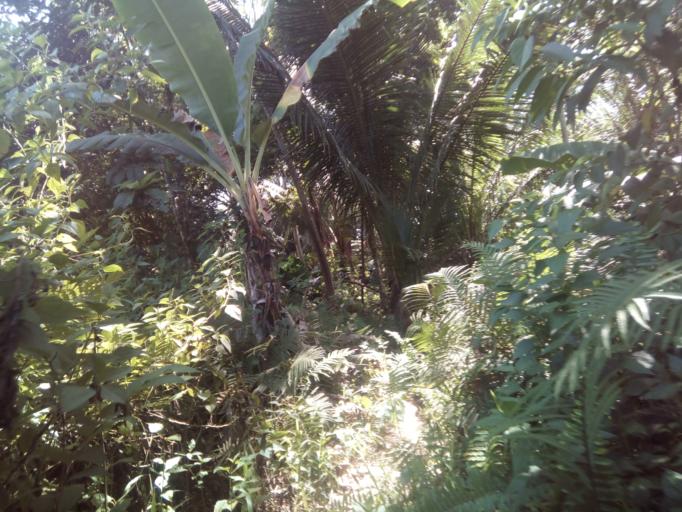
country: PH
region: Caraga
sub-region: Province of Agusan del Sur
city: Santa Josefa
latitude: 7.9539
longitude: 125.9834
